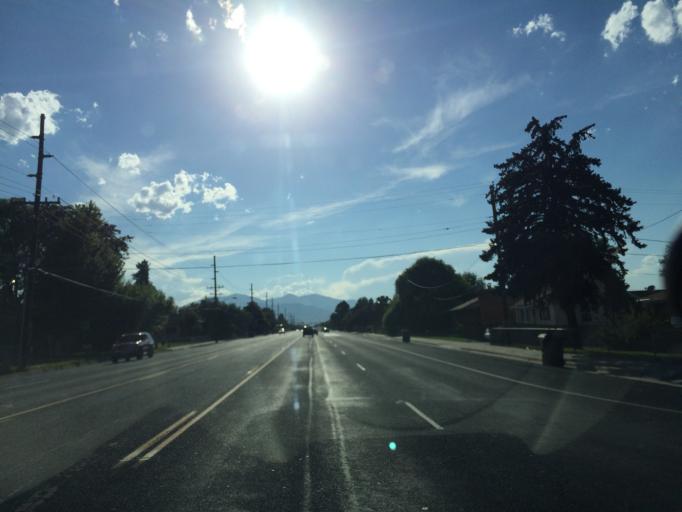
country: US
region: Utah
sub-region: Salt Lake County
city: West Valley City
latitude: 40.6821
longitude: -111.9711
